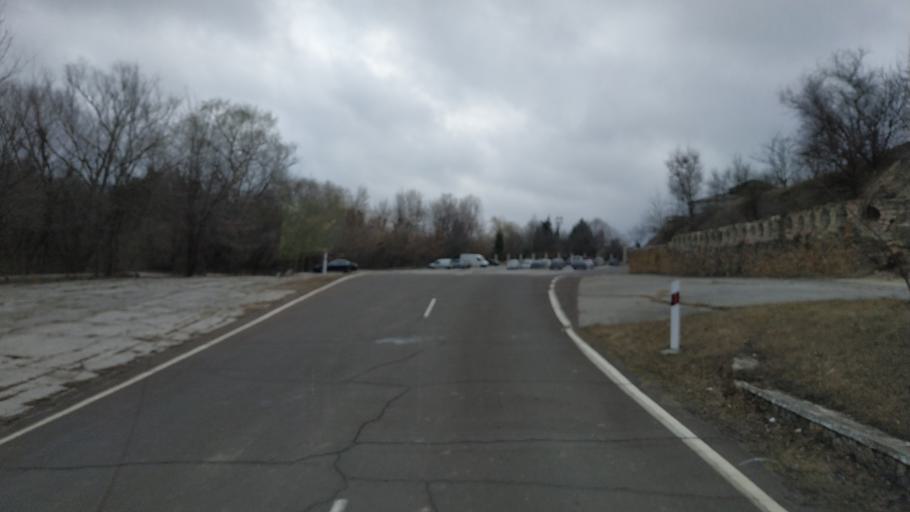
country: MD
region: Laloveni
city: Ialoveni
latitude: 46.9225
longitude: 28.8188
